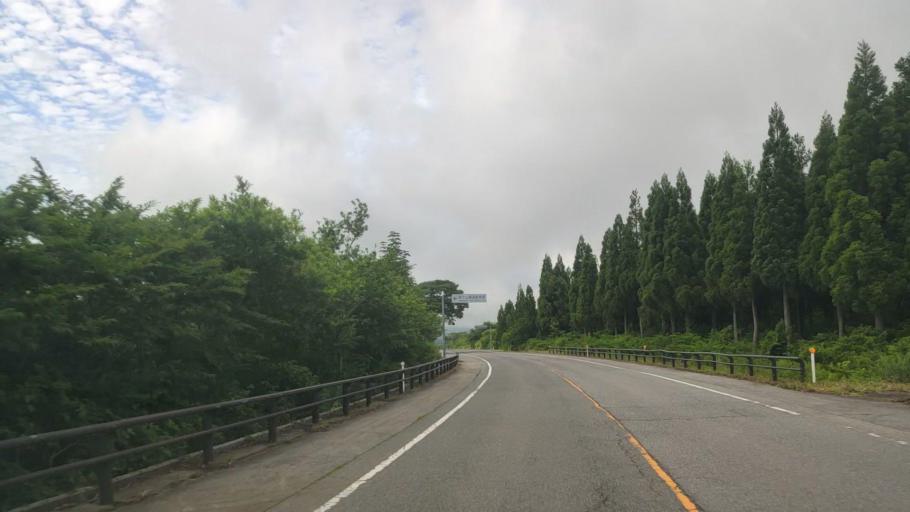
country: JP
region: Tottori
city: Kurayoshi
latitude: 35.3390
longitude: 133.5809
